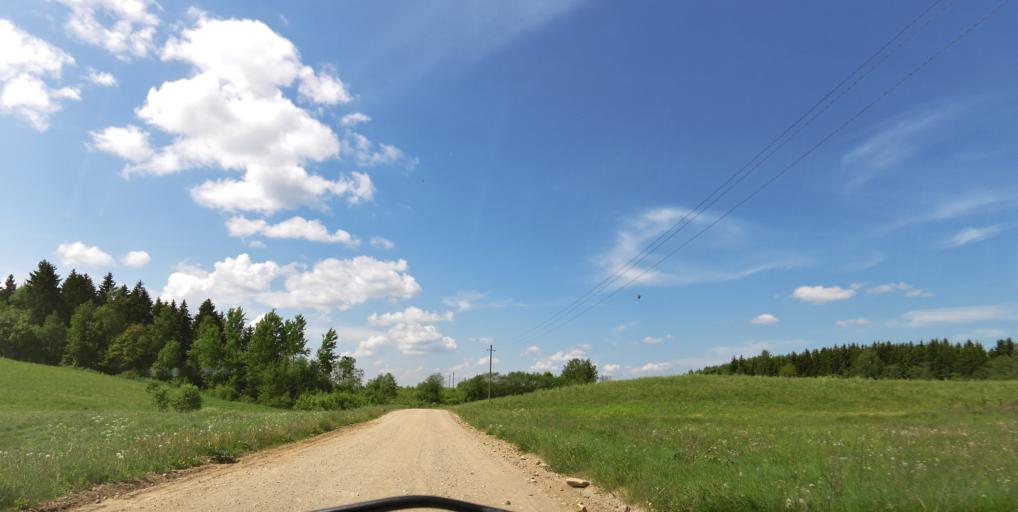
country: LT
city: Grigiskes
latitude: 54.7466
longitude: 25.1175
